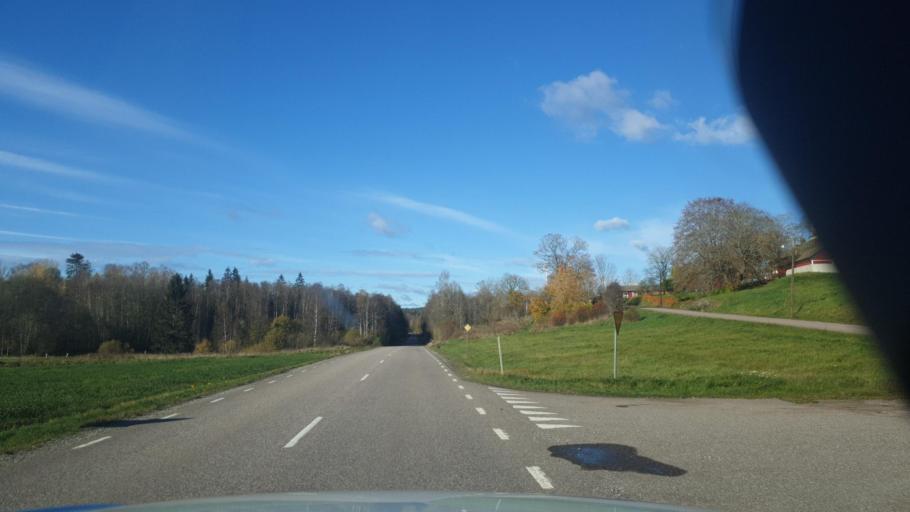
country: SE
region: Vaermland
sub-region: Arvika Kommun
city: Arvika
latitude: 59.6517
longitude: 12.8908
